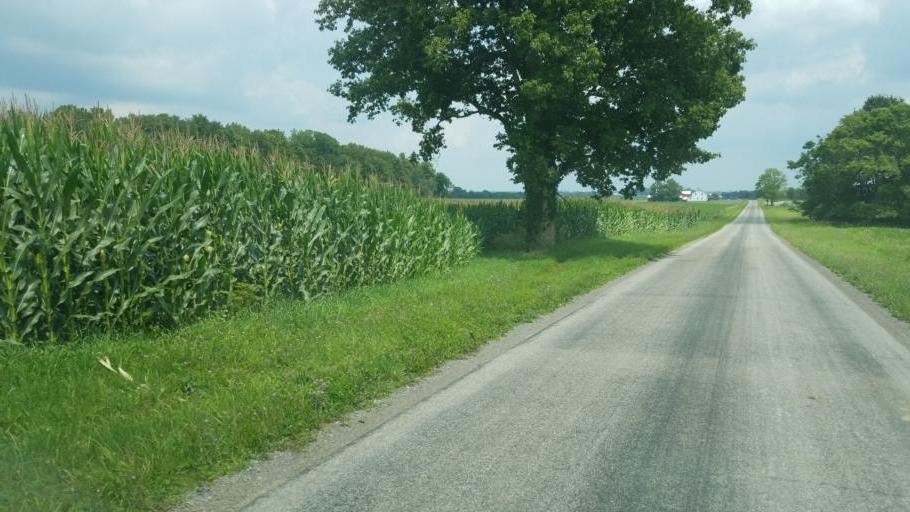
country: US
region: Ohio
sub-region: Hardin County
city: Kenton
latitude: 40.5921
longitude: -83.6367
